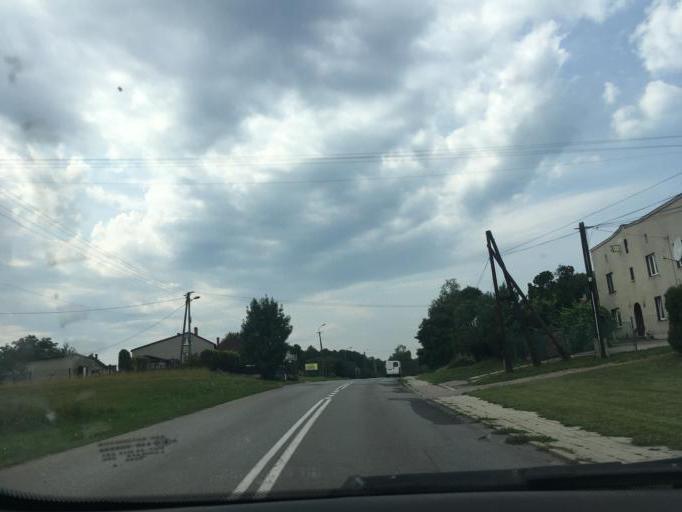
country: PL
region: Silesian Voivodeship
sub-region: Powiat rybnicki
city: Czernica
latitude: 50.0704
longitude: 18.3923
